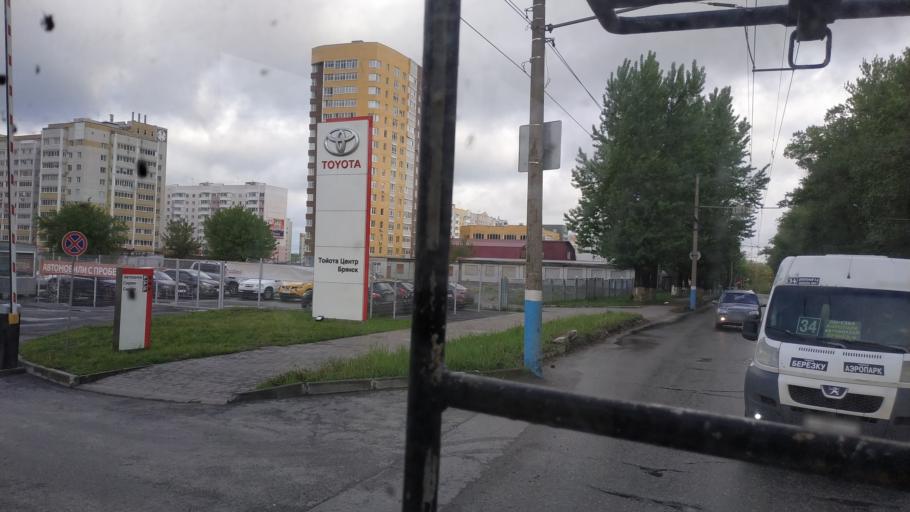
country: RU
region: Brjansk
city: Putevka
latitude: 53.2619
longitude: 34.3247
